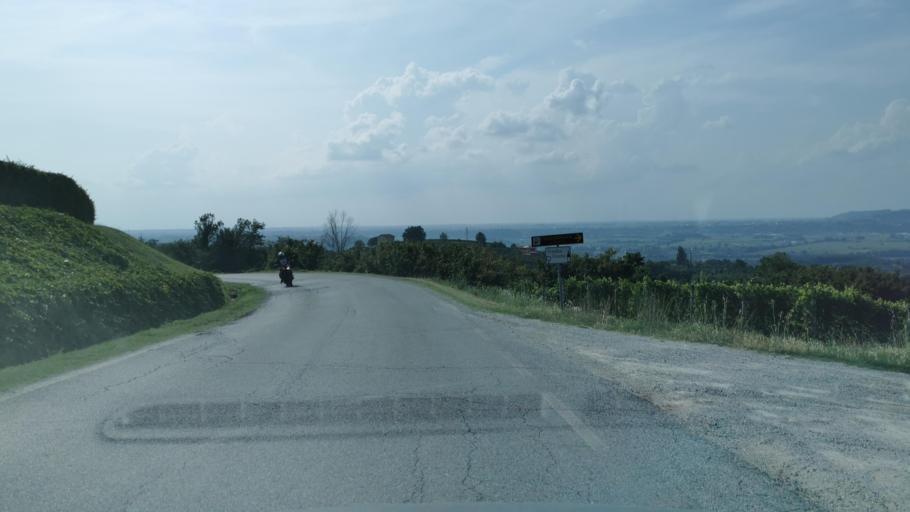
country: IT
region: Piedmont
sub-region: Provincia di Cuneo
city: La Morra
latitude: 44.6446
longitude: 7.9097
